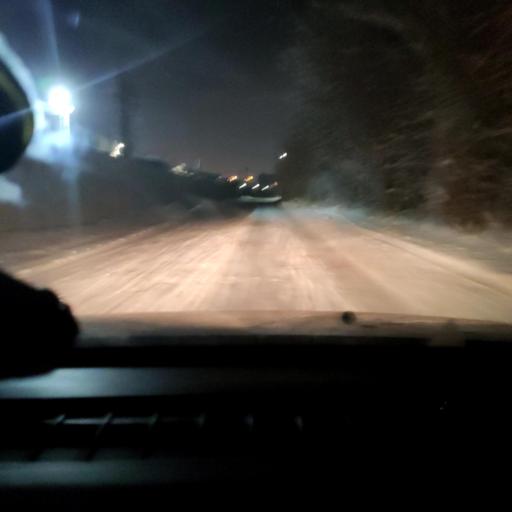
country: RU
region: Samara
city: Samara
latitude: 53.1967
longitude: 50.2344
